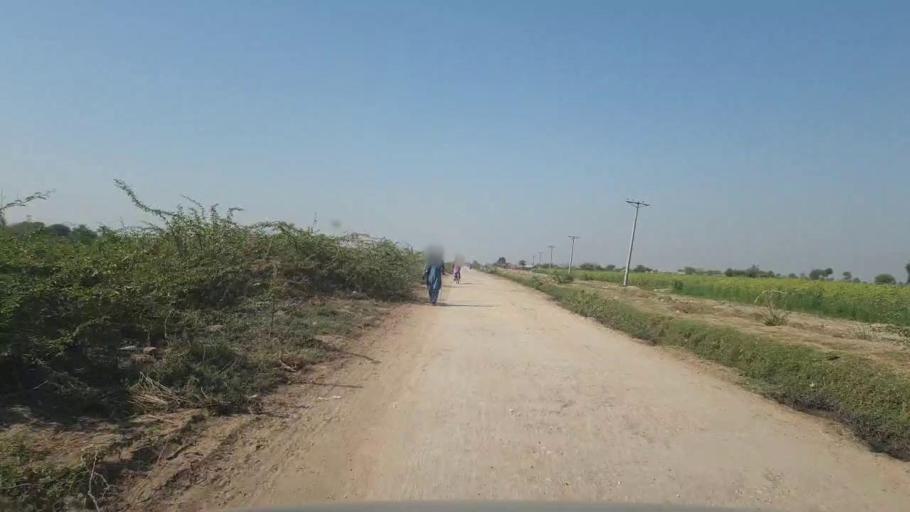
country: PK
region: Sindh
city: Samaro
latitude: 25.2808
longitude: 69.2395
